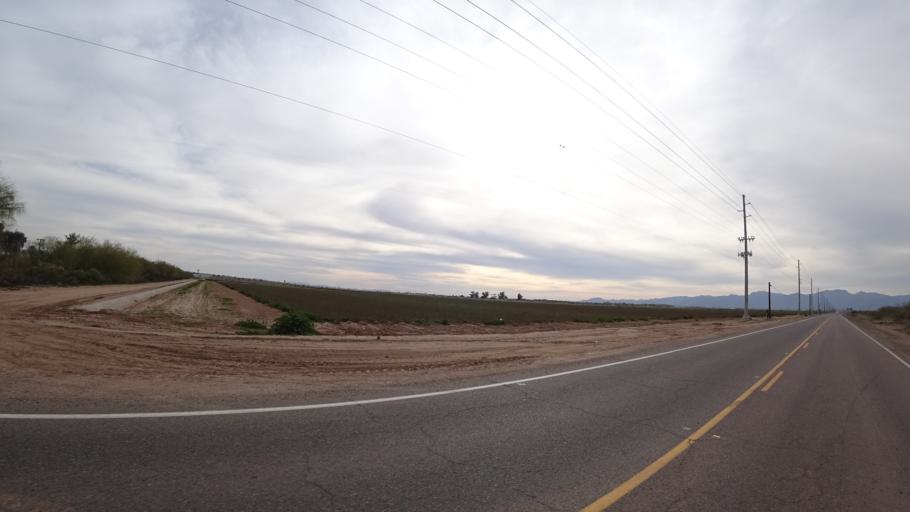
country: US
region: Arizona
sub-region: Maricopa County
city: El Mirage
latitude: 33.5658
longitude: -112.3678
